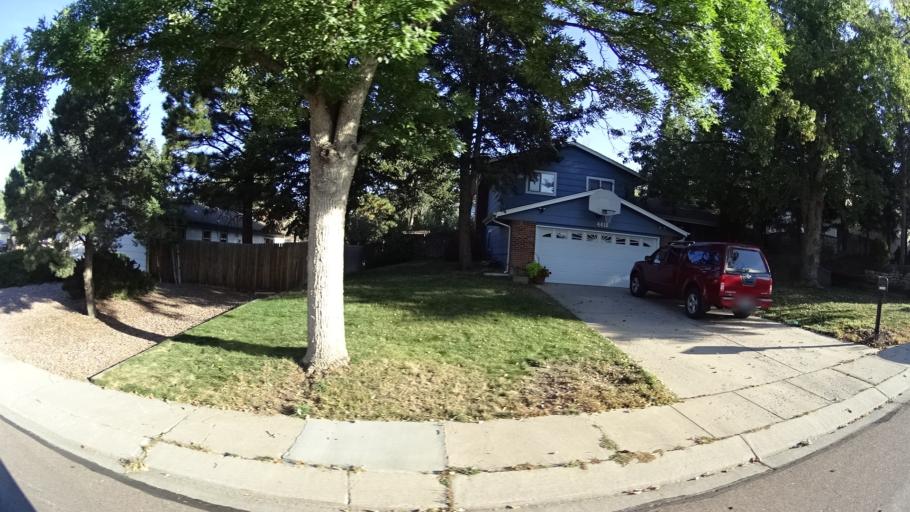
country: US
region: Colorado
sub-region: El Paso County
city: Cimarron Hills
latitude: 38.8832
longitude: -104.7449
